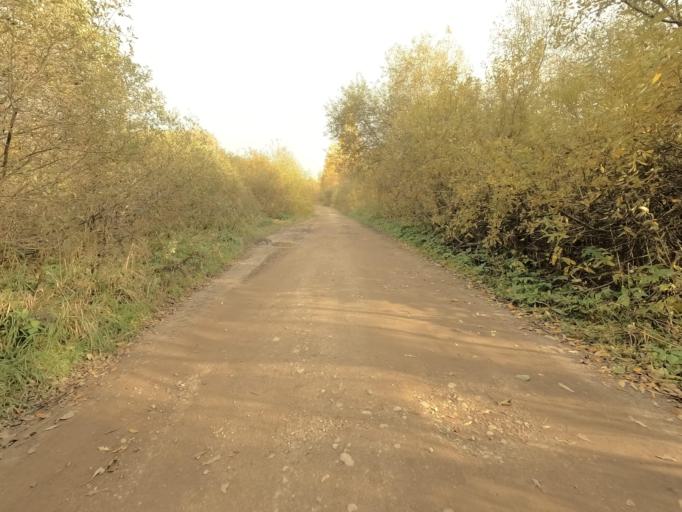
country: RU
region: Novgorod
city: Volkhovskiy
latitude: 58.8933
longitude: 31.0218
